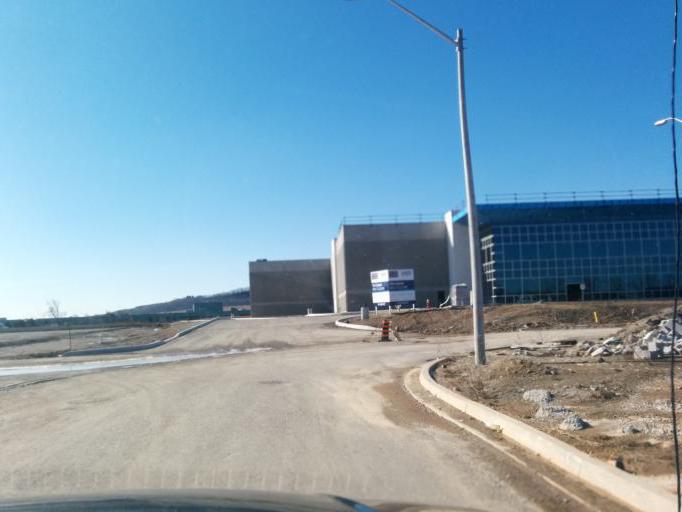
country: CA
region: Ontario
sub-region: Halton
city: Milton
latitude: 43.5277
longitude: -79.9220
